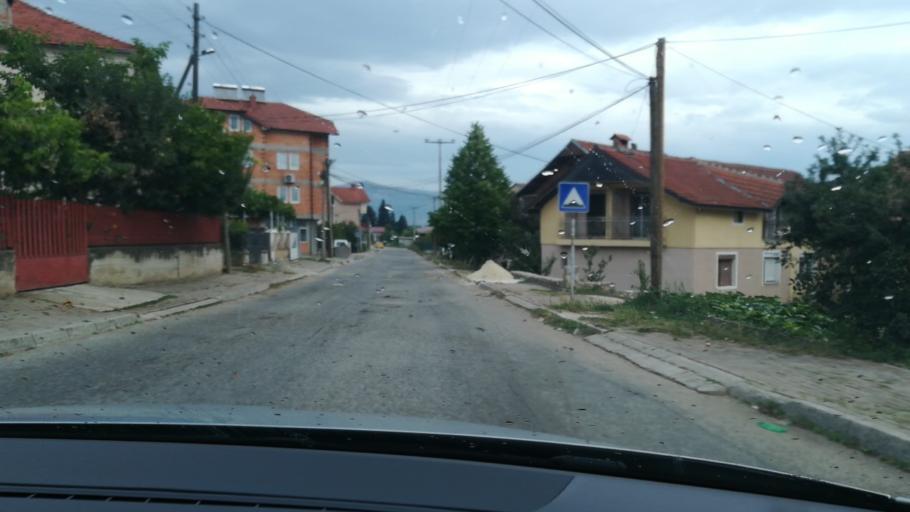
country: MK
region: Kicevo
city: Kicevo
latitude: 41.5099
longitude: 20.9481
